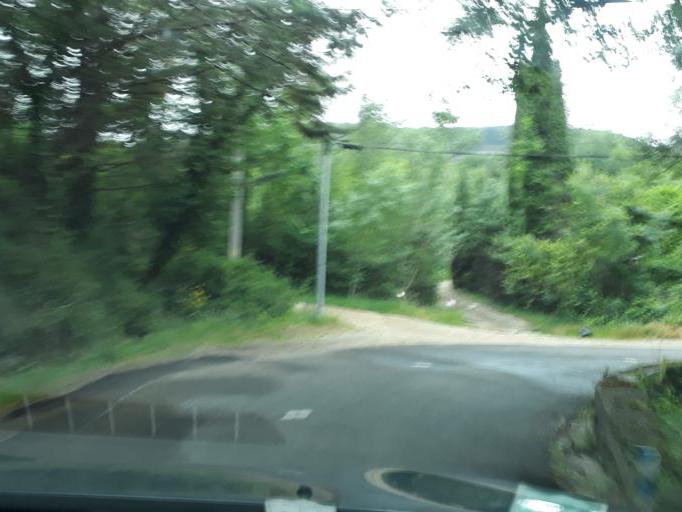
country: FR
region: Languedoc-Roussillon
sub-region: Departement de l'Herault
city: Lodeve
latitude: 43.7613
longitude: 3.3187
